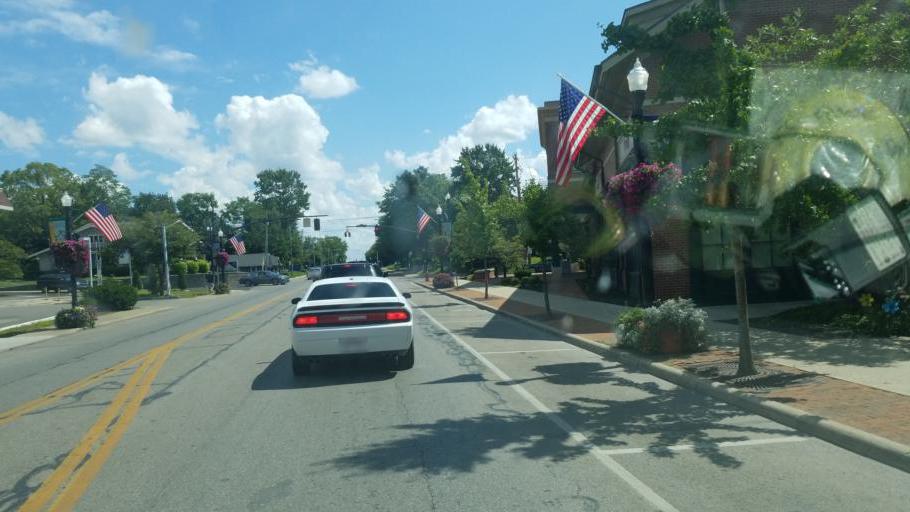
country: US
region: Ohio
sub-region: Franklin County
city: Westerville
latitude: 40.1223
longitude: -82.9303
